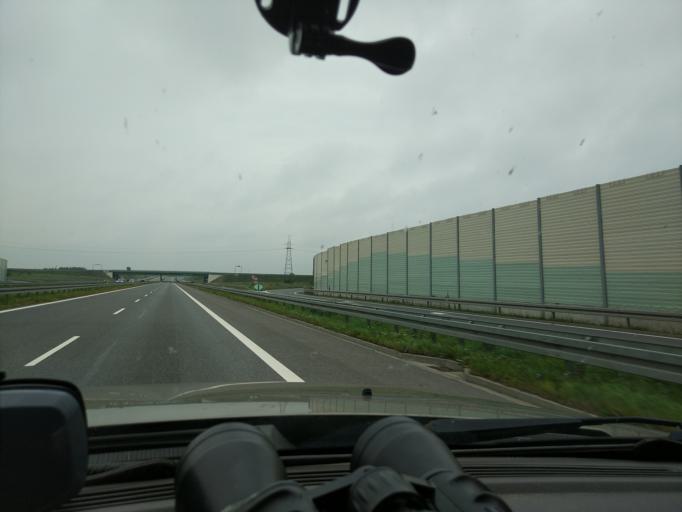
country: PL
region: Podlasie
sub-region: Powiat zambrowski
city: Zambrow
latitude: 52.9768
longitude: 22.2108
